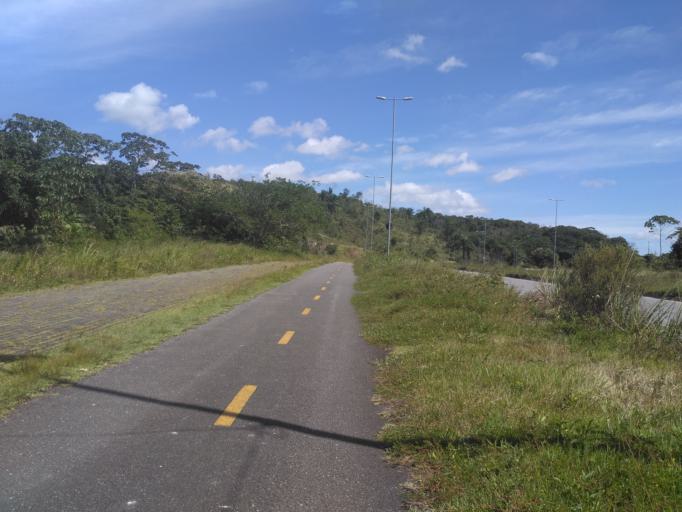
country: BR
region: Pernambuco
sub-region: Sao Lourenco Da Mata
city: Sao Lourenco da Mata
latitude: -8.0445
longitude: -35.0015
